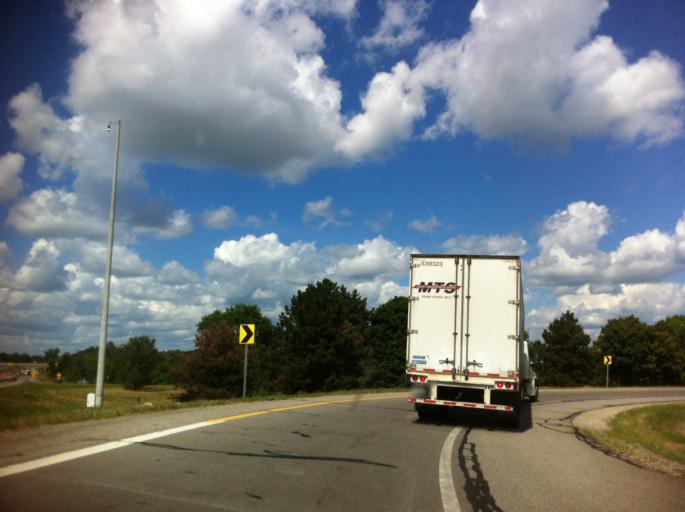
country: US
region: Michigan
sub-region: Washtenaw County
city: Ypsilanti
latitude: 42.2263
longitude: -83.6850
